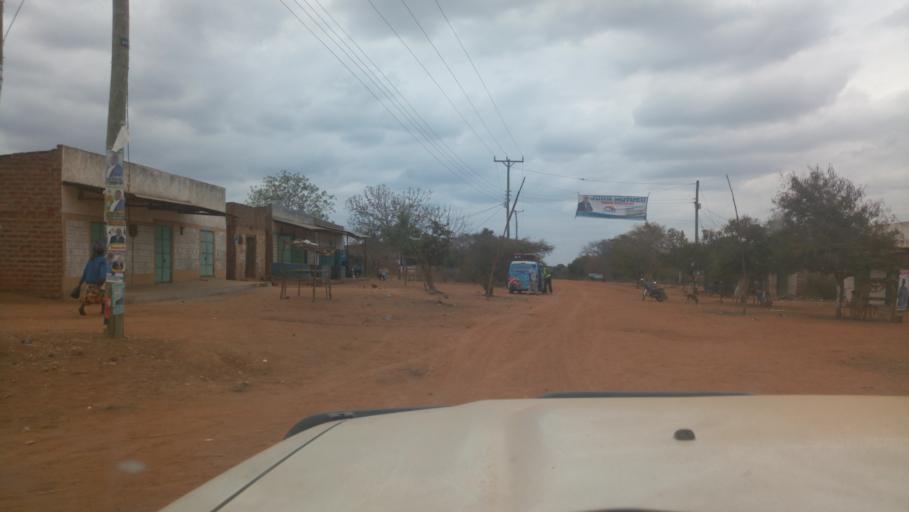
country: KE
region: Makueni
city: Wote
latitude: -1.6329
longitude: 37.8730
